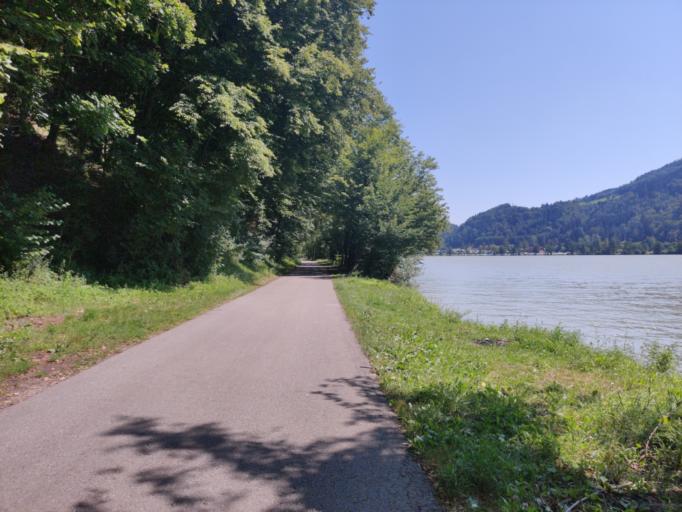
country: AT
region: Upper Austria
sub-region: Politischer Bezirk Rohrbach
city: Pfarrkirchen im Muehlkreis
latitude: 48.4305
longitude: 13.8580
